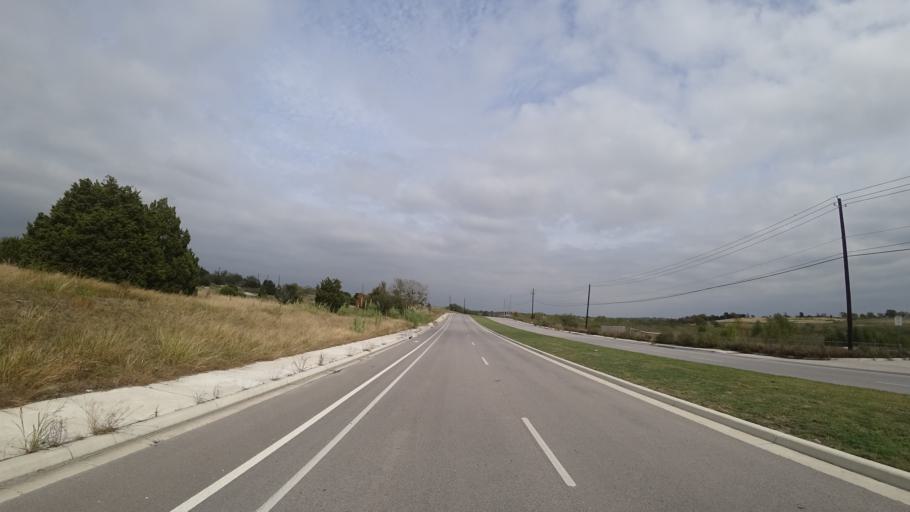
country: US
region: Texas
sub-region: Travis County
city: Pflugerville
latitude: 30.3794
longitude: -97.6077
